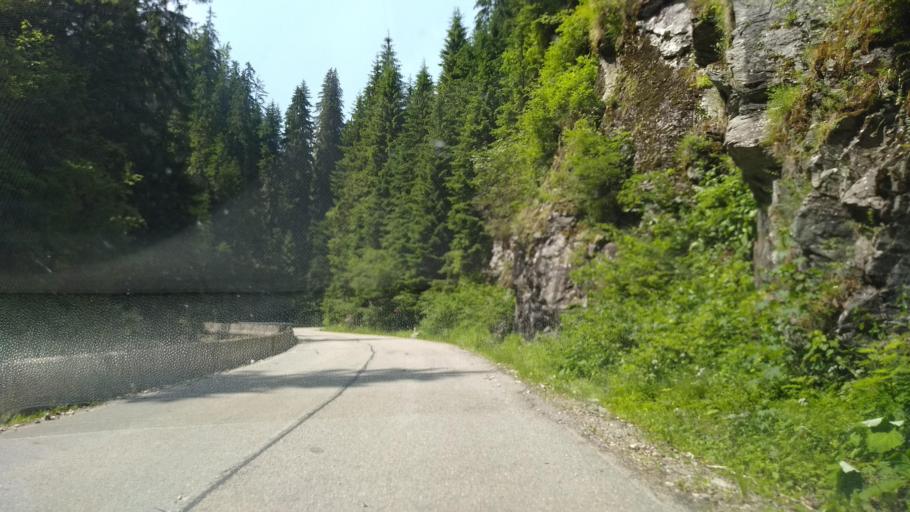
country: RO
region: Gorj
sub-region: Comuna Runcu
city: Valea Mare
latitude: 45.2723
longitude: 22.9571
